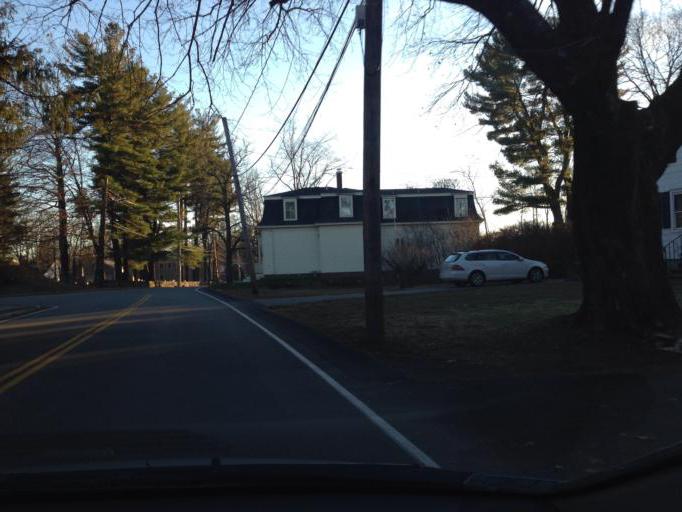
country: US
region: Massachusetts
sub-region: Middlesex County
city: Bedford
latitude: 42.4937
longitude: -71.2785
